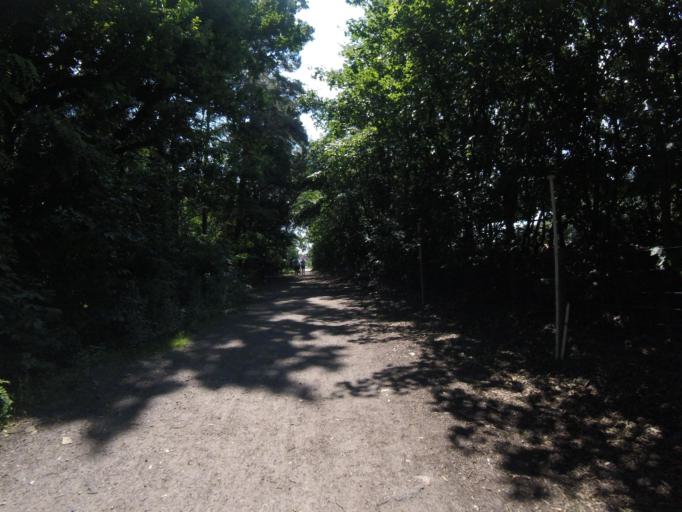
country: DE
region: Brandenburg
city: Wildau
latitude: 52.3264
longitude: 13.6165
